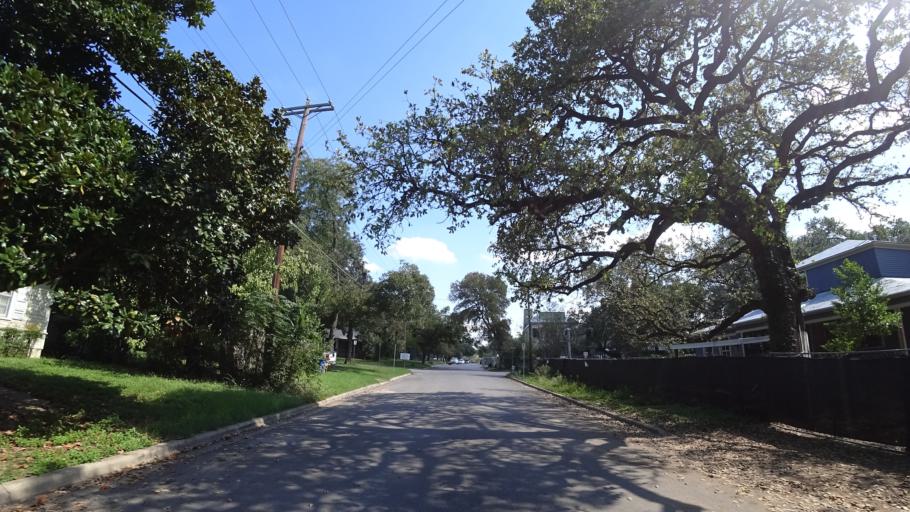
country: US
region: Texas
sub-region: Travis County
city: Austin
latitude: 30.3085
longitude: -97.7447
